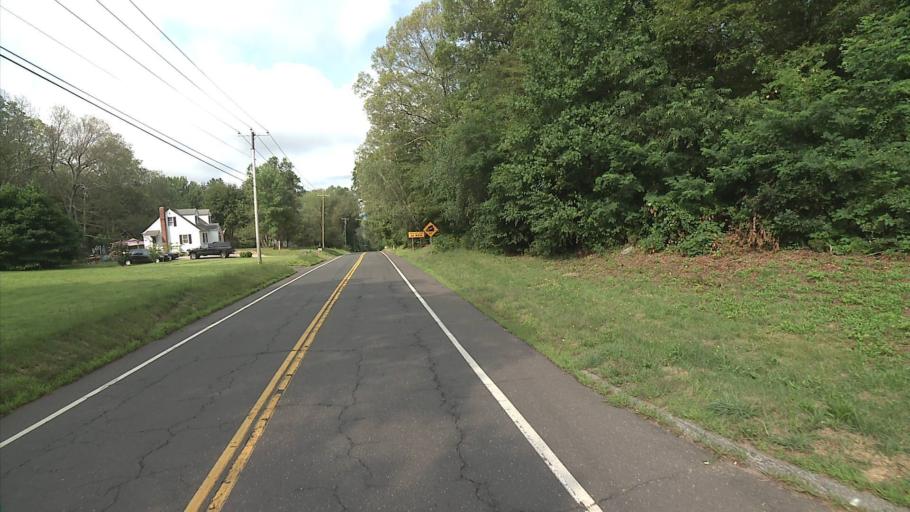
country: US
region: Connecticut
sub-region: Middlesex County
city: Moodus
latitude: 41.5205
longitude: -72.4163
